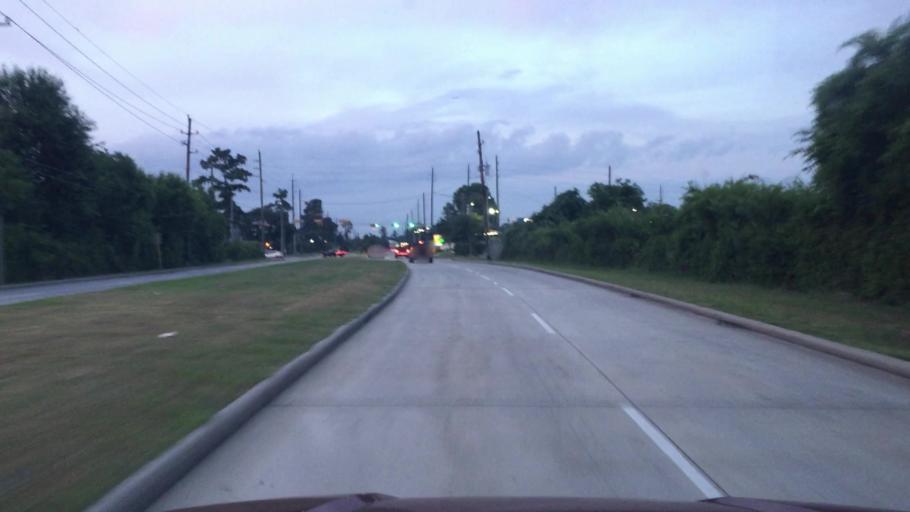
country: US
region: Texas
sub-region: Harris County
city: Tomball
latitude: 30.0474
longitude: -95.5388
